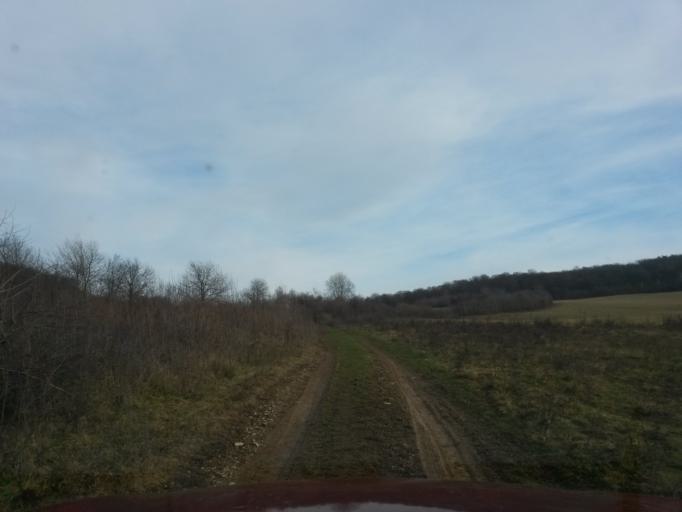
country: SK
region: Kosicky
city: Dobsina
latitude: 48.7433
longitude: 20.3825
